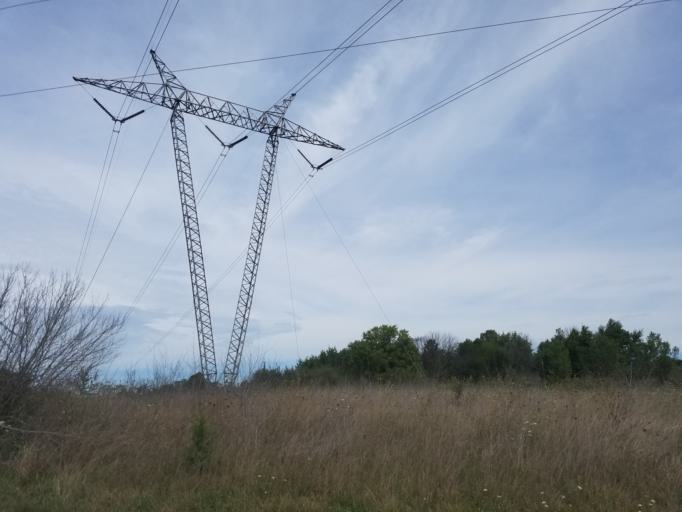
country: US
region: Ohio
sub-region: Richland County
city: Lexington
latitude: 40.5721
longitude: -82.6376
